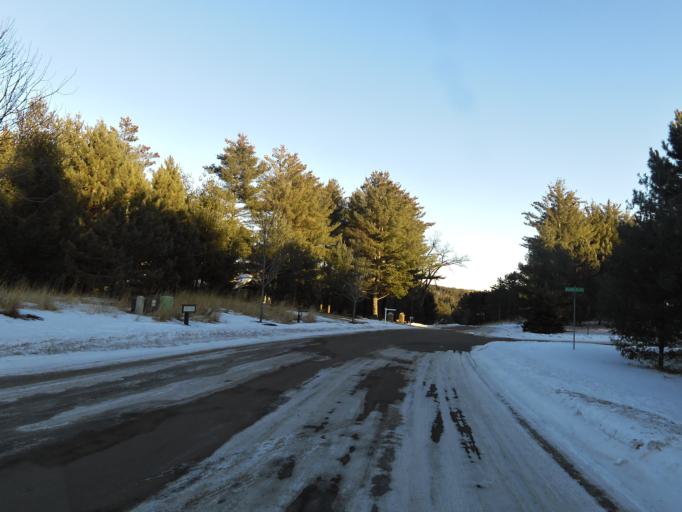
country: US
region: Minnesota
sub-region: Washington County
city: Lake Elmo
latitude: 44.9832
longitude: -92.8391
